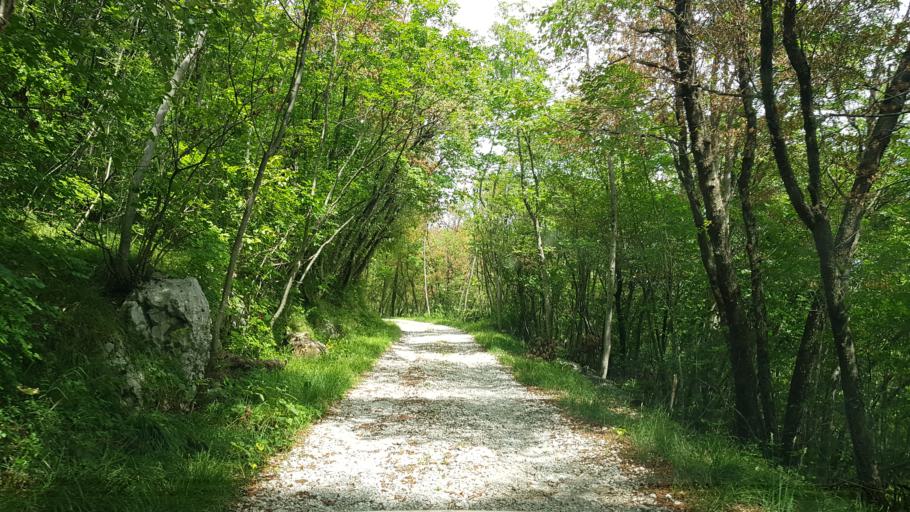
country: SI
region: Nova Gorica
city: Solkan
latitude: 46.0111
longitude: 13.6414
